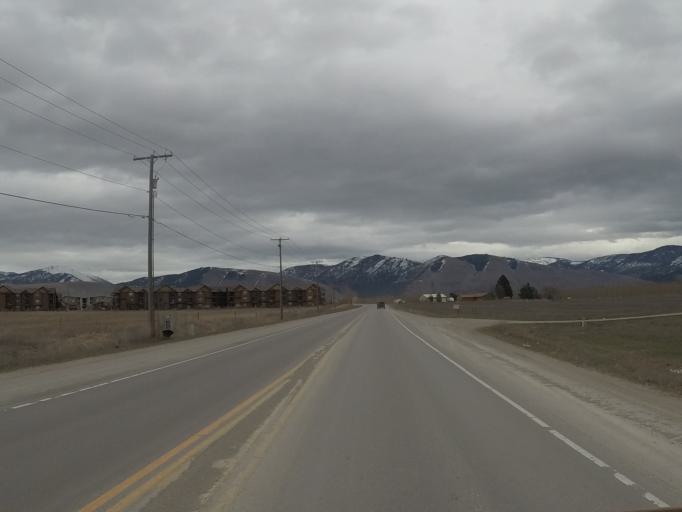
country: US
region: Montana
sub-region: Missoula County
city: Orchard Homes
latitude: 46.8872
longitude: -114.0542
